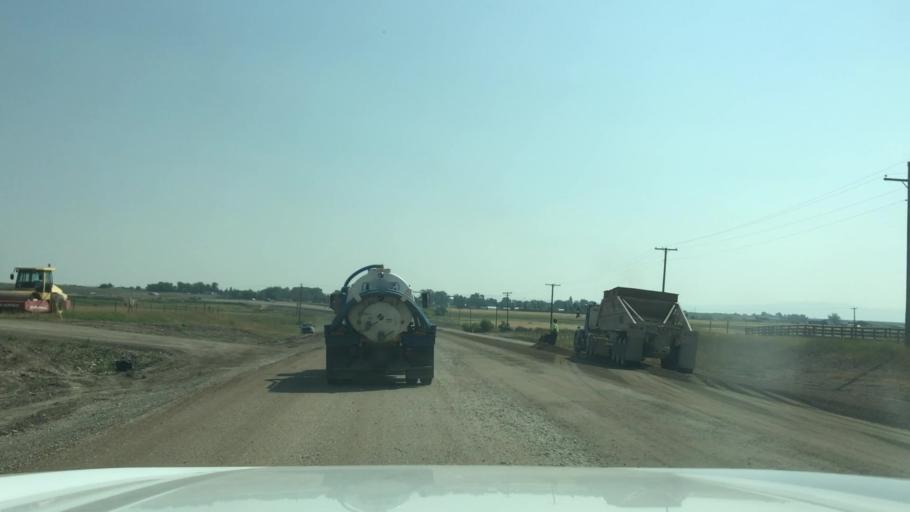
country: US
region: Montana
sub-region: Judith Basin County
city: Stanford
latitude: 47.0126
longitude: -109.8720
